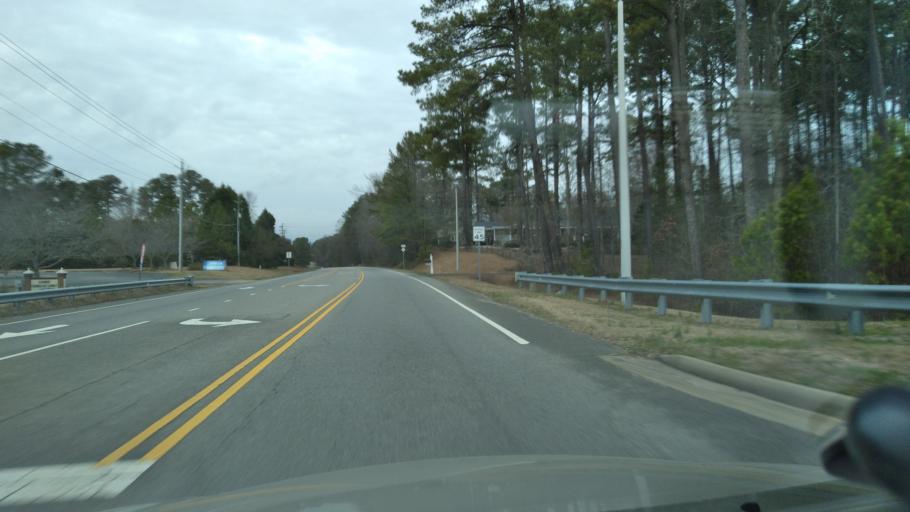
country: US
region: North Carolina
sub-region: Wake County
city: Garner
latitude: 35.6894
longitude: -78.6050
